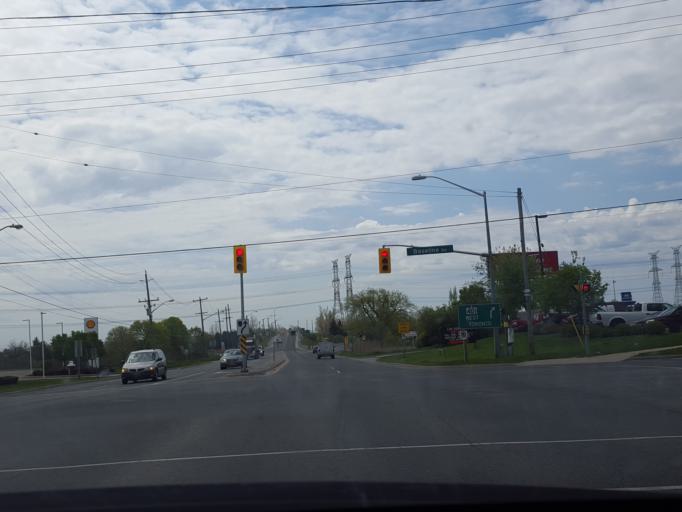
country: CA
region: Ontario
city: Oshawa
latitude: 43.8979
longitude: -78.6910
